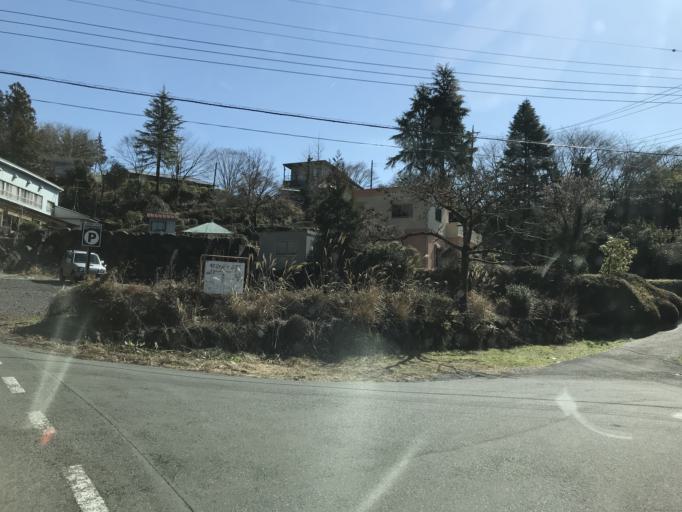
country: JP
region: Shizuoka
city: Fujinomiya
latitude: 35.2608
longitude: 138.6664
